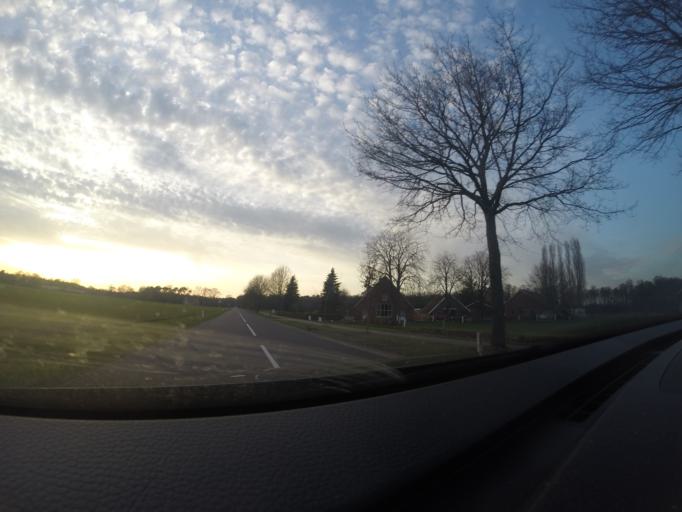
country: NL
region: Overijssel
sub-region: Gemeente Haaksbergen
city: Haaksbergen
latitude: 52.1492
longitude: 6.7939
